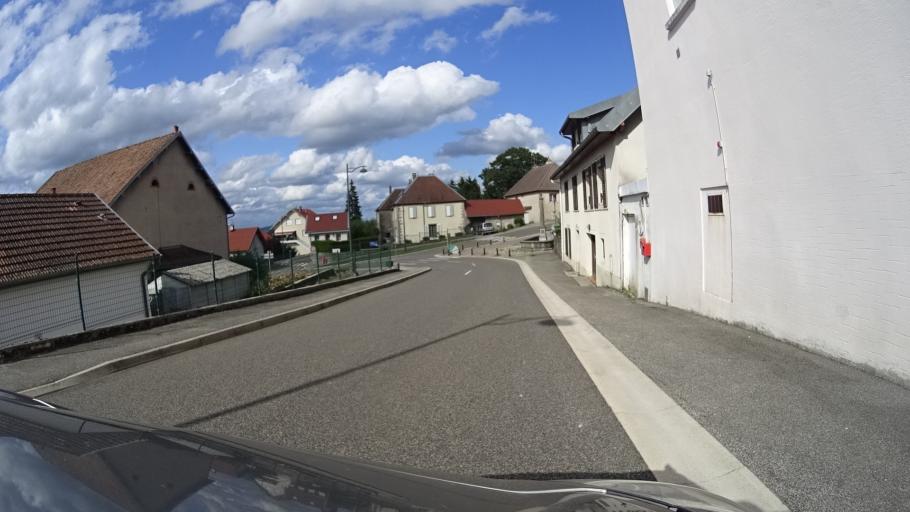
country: FR
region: Franche-Comte
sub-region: Departement du Doubs
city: Mamirolle
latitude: 47.1973
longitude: 6.1627
